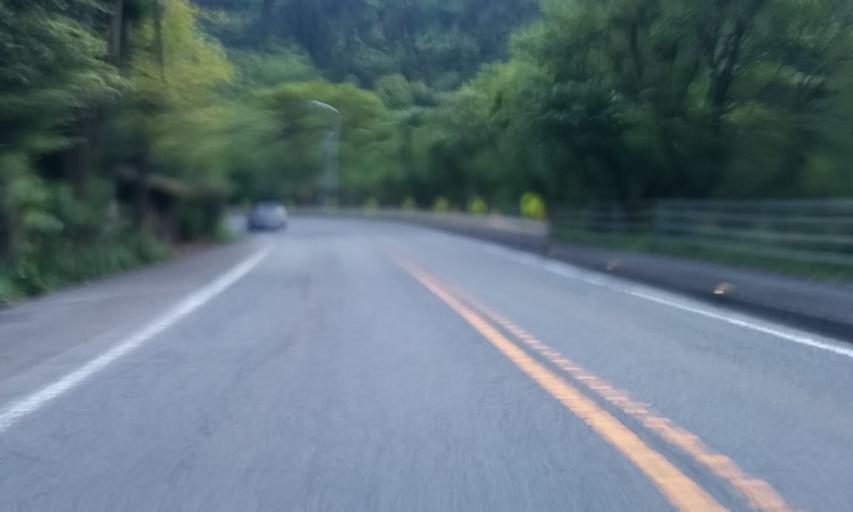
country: JP
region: Ehime
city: Saijo
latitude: 33.8509
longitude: 133.0022
